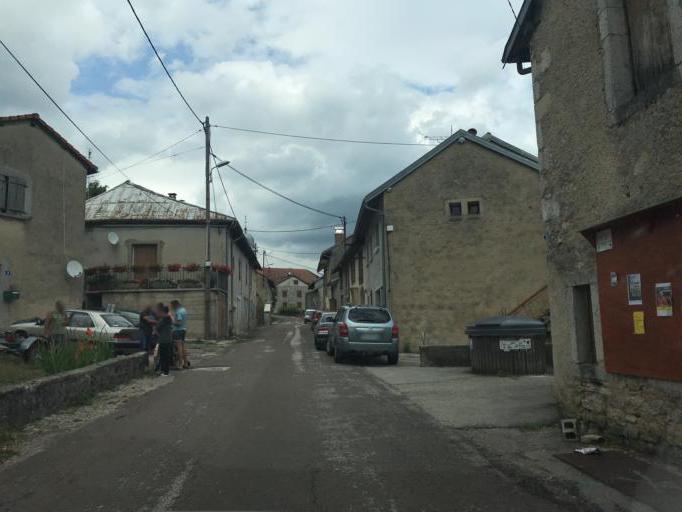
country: FR
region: Franche-Comte
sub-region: Departement du Jura
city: Valfin-les-Saint-Claude
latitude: 46.4372
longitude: 5.8546
